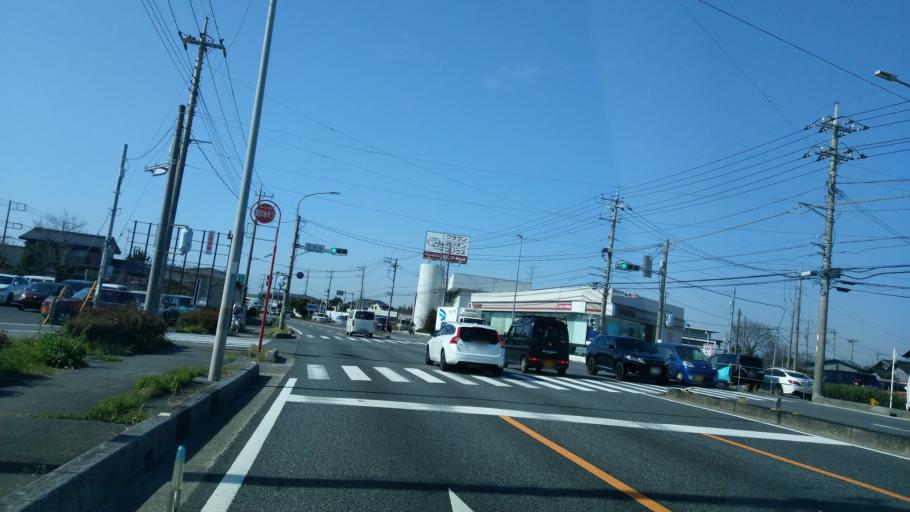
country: JP
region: Saitama
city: Sakado
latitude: 36.0130
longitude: 139.4347
